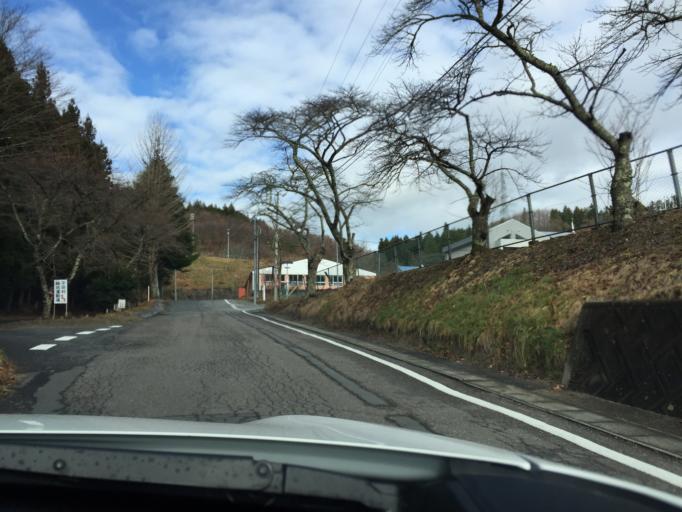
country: JP
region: Fukushima
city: Ishikawa
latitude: 37.2210
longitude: 140.5754
